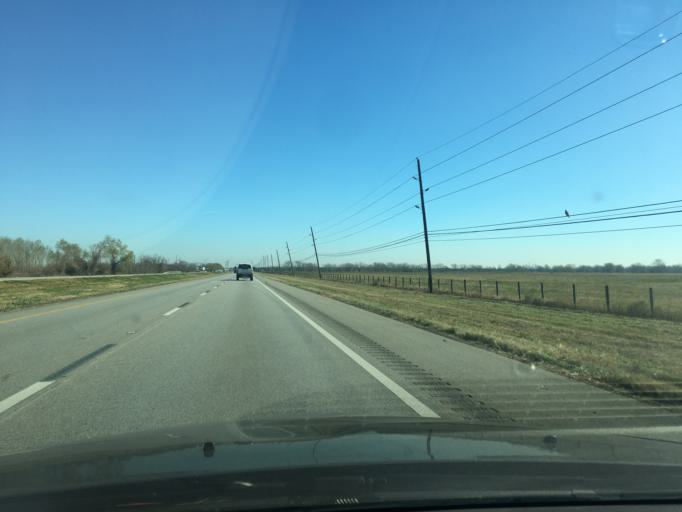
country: US
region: Texas
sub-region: Fort Bend County
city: Pecan Grove
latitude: 29.5980
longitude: -95.7194
